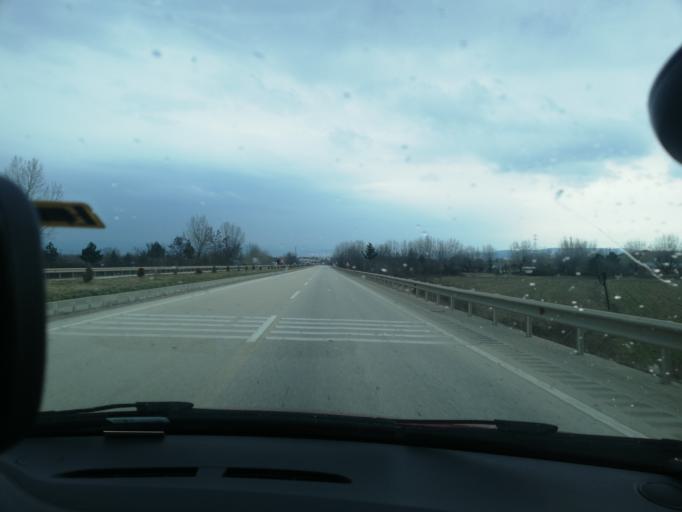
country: TR
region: Kastamonu
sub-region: Cide
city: Kastamonu
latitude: 41.4881
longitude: 33.7623
